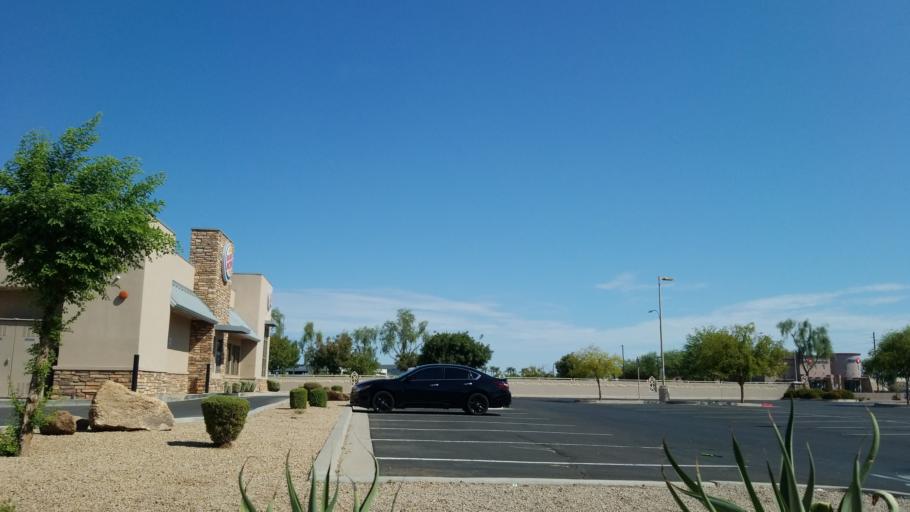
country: US
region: Arizona
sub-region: Maricopa County
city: Tolleson
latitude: 33.4222
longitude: -112.2227
